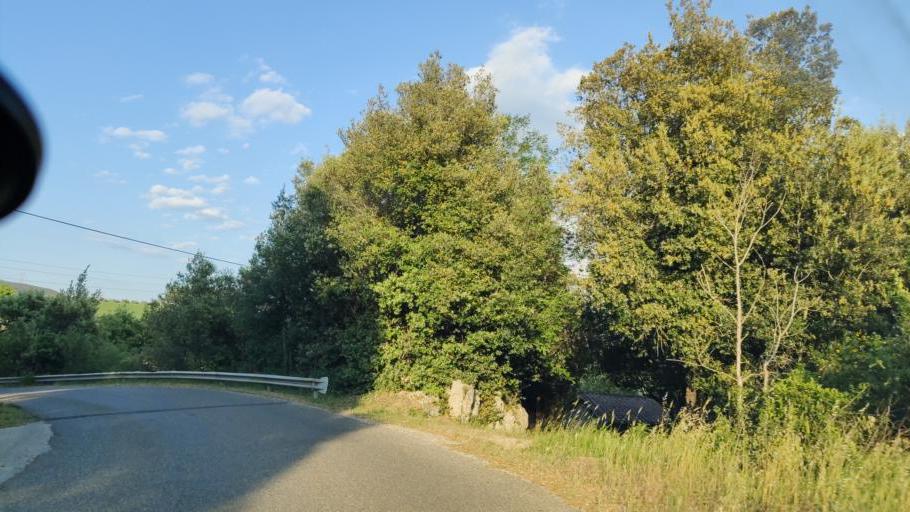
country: IT
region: Umbria
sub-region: Provincia di Terni
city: Amelia
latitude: 42.5808
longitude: 12.3890
